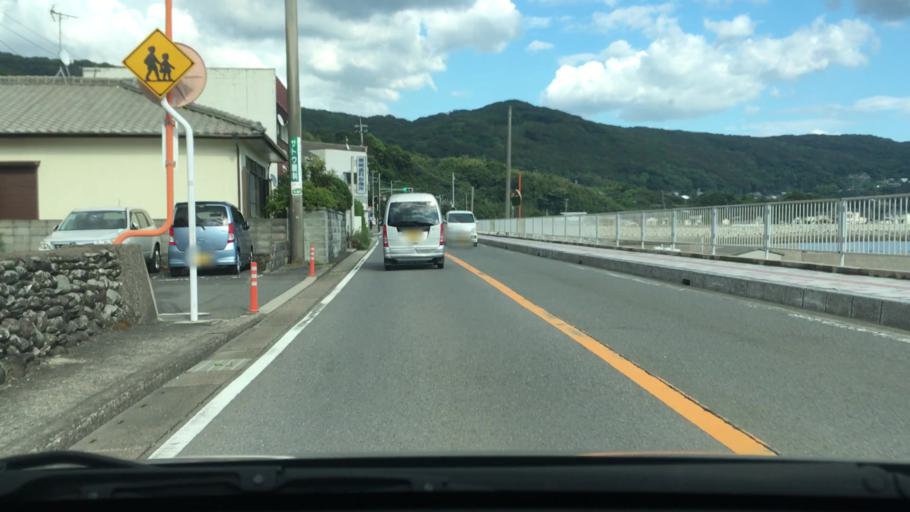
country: JP
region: Nagasaki
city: Togitsu
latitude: 32.8354
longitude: 129.7147
